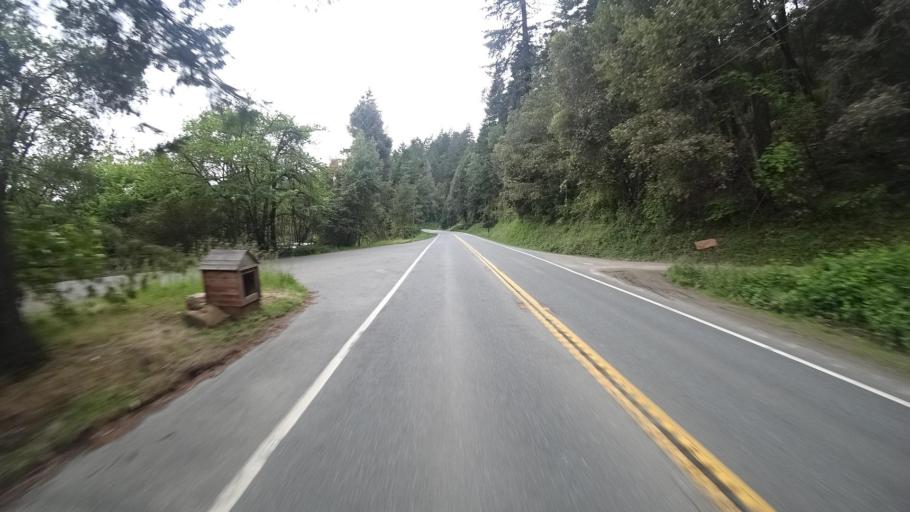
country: US
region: California
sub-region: Humboldt County
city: Willow Creek
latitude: 40.9863
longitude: -123.6382
